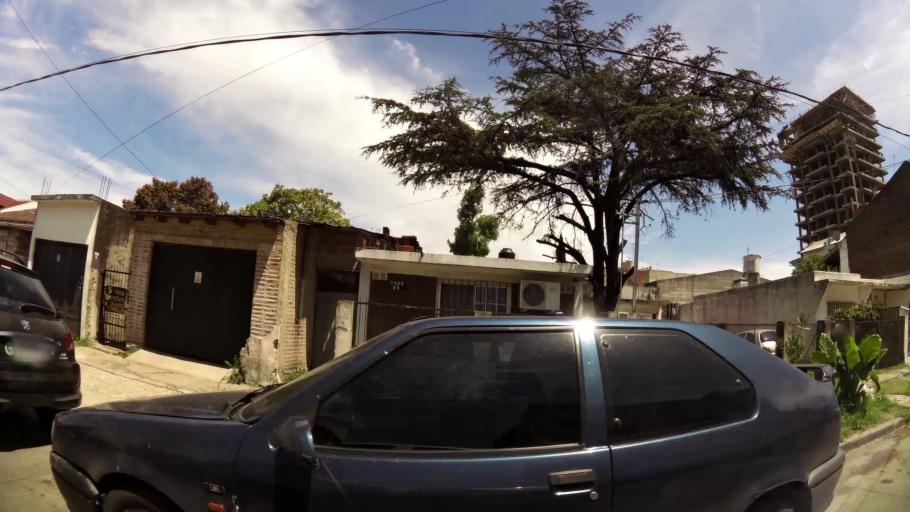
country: AR
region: Buenos Aires
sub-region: Partido de Quilmes
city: Quilmes
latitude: -34.7821
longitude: -58.2637
